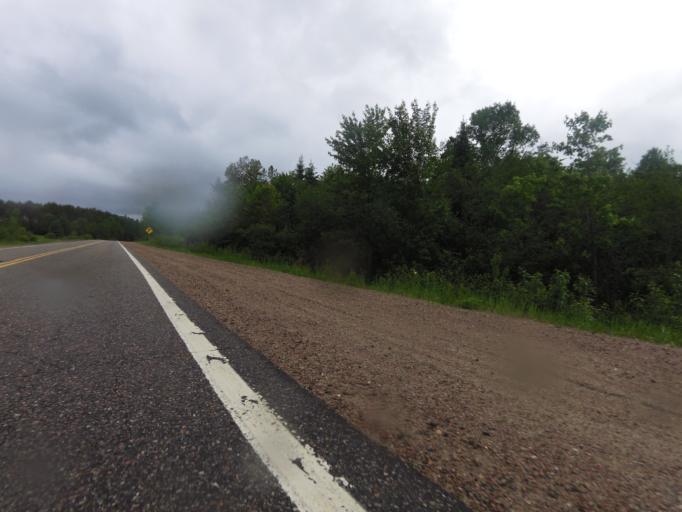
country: CA
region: Quebec
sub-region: Outaouais
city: Shawville
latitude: 45.9160
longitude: -76.2565
